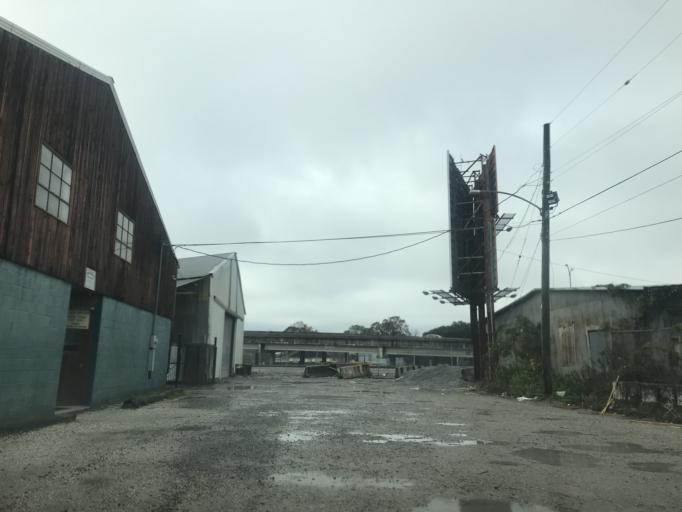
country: US
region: Louisiana
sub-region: Orleans Parish
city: New Orleans
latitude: 29.9738
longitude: -90.1099
